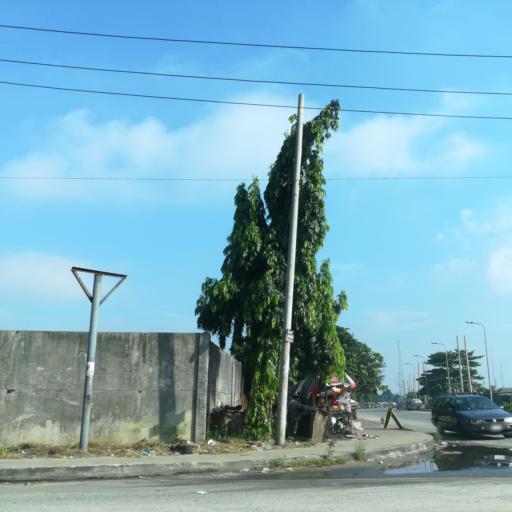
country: NG
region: Rivers
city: Port Harcourt
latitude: 4.8016
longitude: 7.0241
